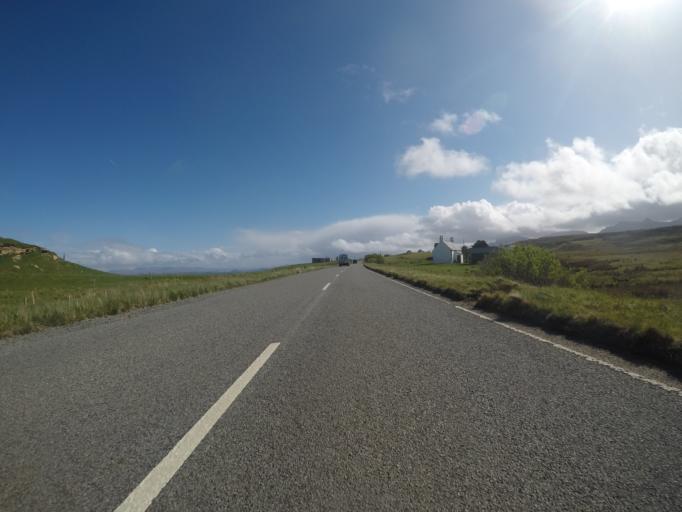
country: GB
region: Scotland
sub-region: Highland
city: Portree
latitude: 57.5991
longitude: -6.1636
